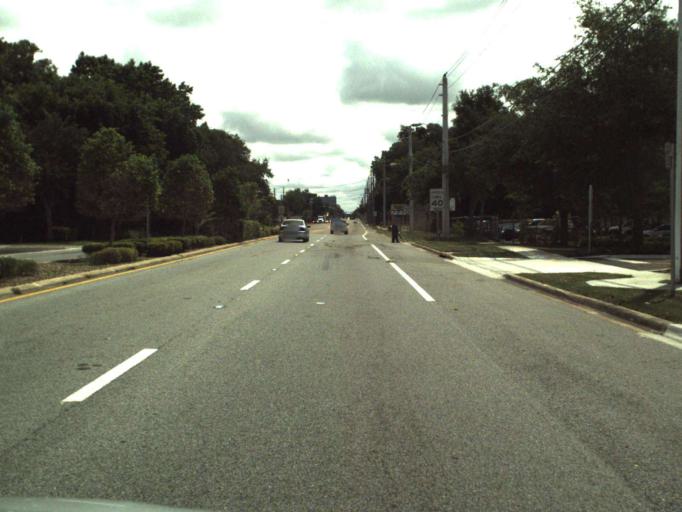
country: US
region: Florida
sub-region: Seminole County
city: Sanford
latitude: 28.8116
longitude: -81.2821
